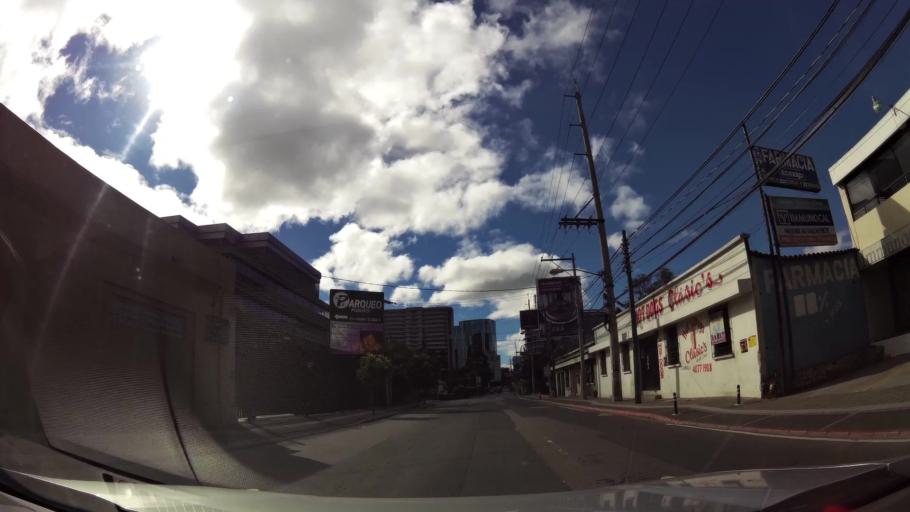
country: GT
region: Guatemala
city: Guatemala City
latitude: 14.6065
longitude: -90.5103
